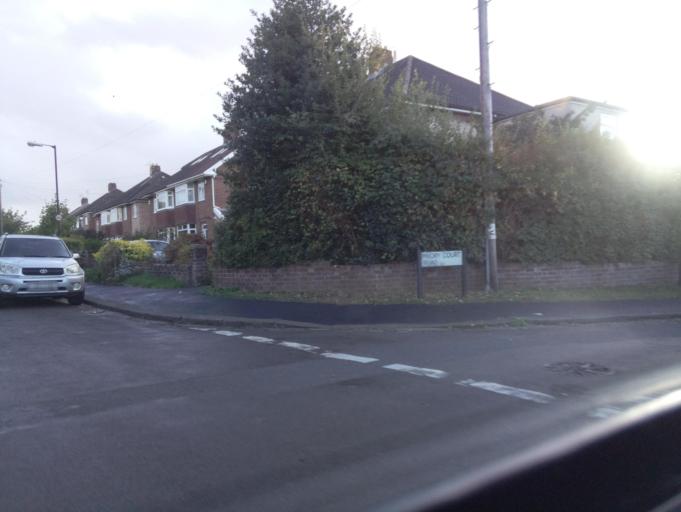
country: GB
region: England
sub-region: Bristol
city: Bristol
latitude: 51.4920
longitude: -2.6122
